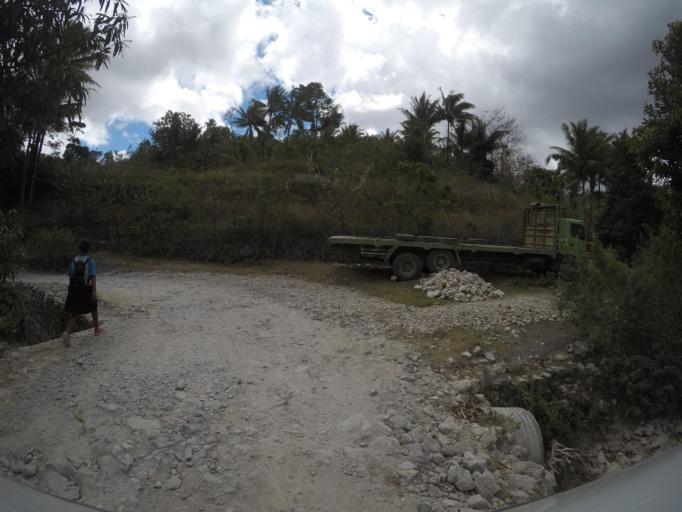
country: TL
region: Baucau
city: Baucau
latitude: -8.5246
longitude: 126.6894
